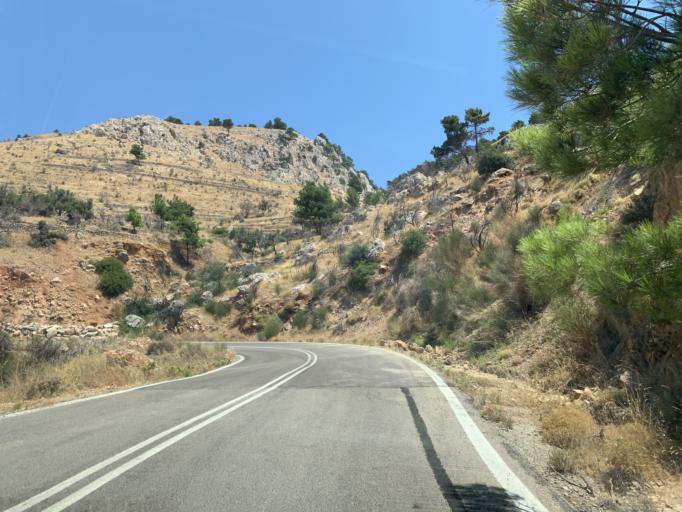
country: GR
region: North Aegean
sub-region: Chios
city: Vrontados
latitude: 38.4504
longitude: 25.9783
